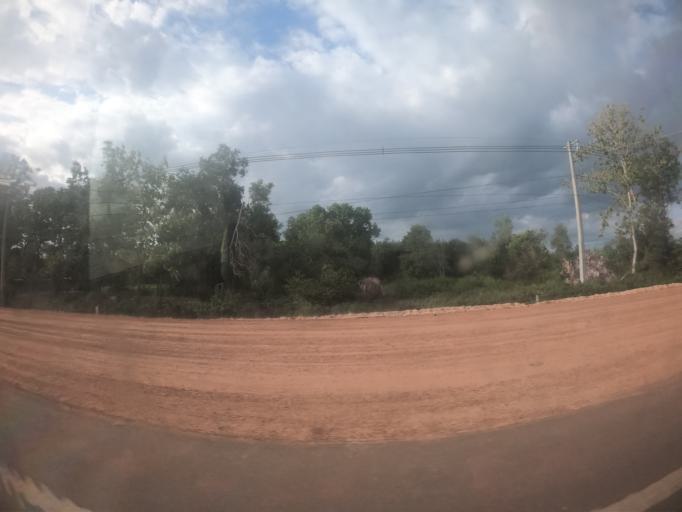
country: TH
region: Surin
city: Kap Choeng
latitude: 14.4730
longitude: 103.6069
